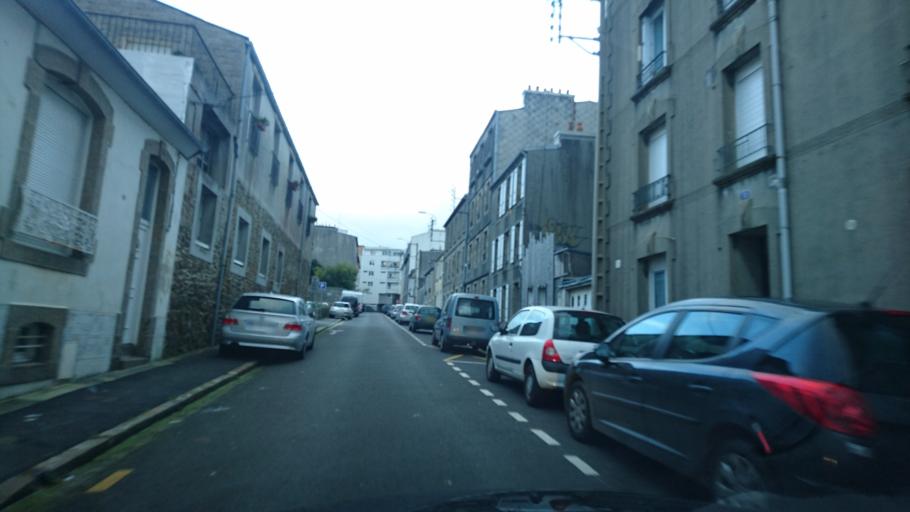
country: FR
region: Brittany
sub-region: Departement du Finistere
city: Brest
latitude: 48.3958
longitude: -4.4716
